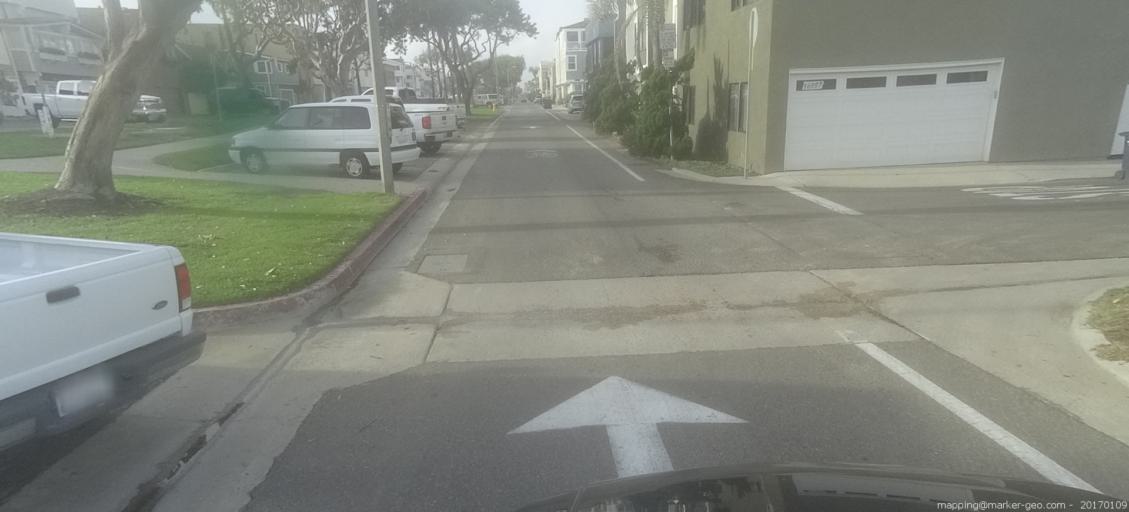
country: US
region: California
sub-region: Orange County
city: Seal Beach
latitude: 33.7151
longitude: -118.0681
